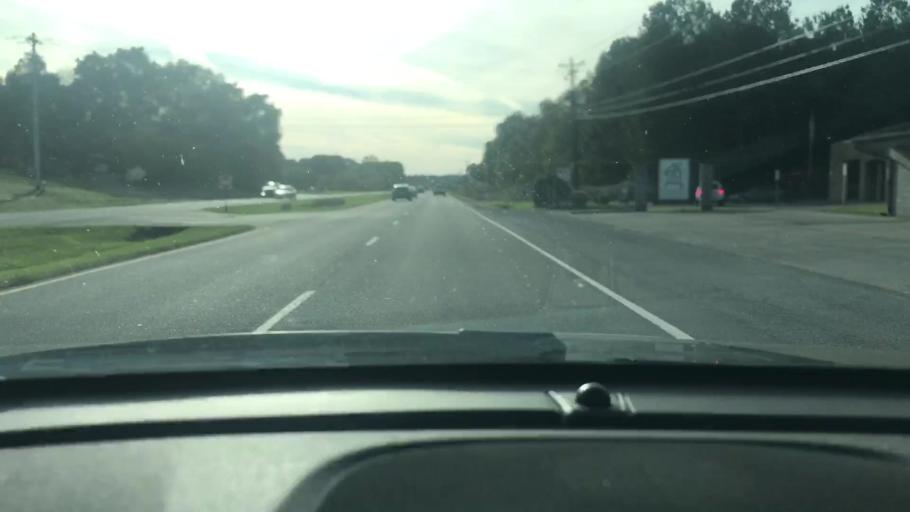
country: US
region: Tennessee
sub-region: Williamson County
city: Fairview
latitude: 35.9859
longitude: -87.1093
